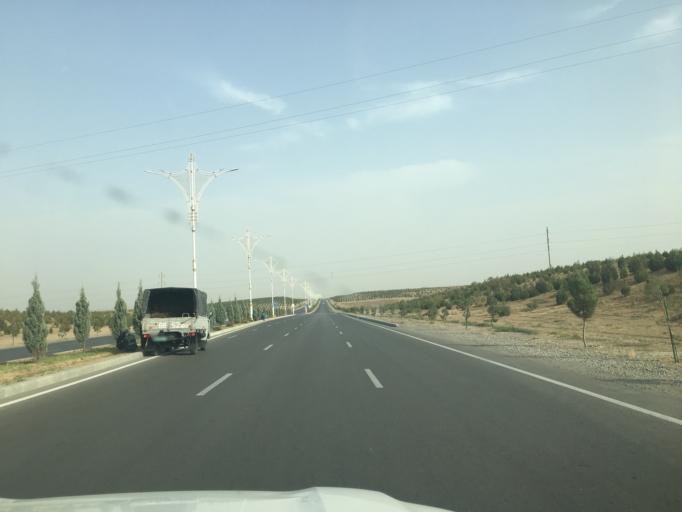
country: TM
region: Ahal
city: Annau
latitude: 37.8778
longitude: 58.4310
